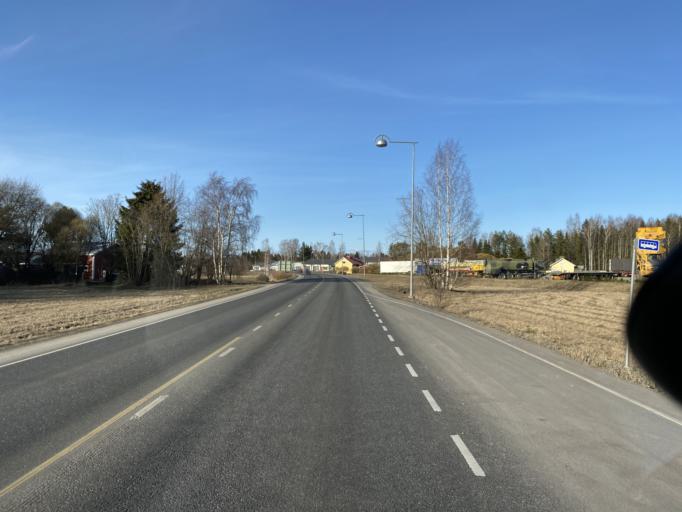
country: FI
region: Satakunta
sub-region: Pori
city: Huittinen
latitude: 61.1668
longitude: 22.7067
